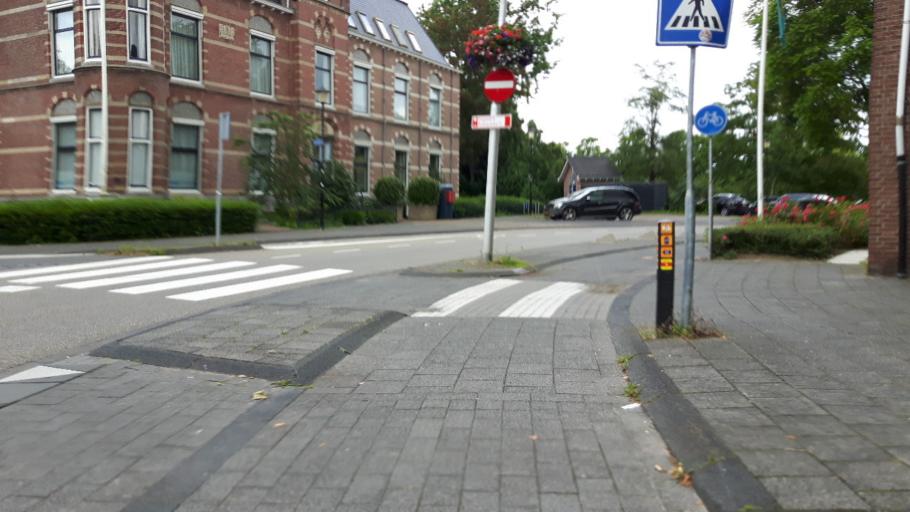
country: NL
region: Utrecht
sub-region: Gemeente Woerden
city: Woerden
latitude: 52.0876
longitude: 4.8832
